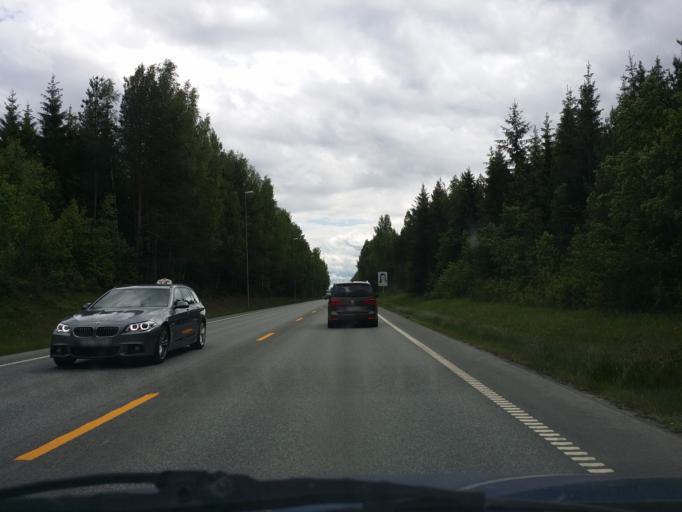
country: NO
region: Hedmark
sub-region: Stange
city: Stange
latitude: 60.7537
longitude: 11.1950
